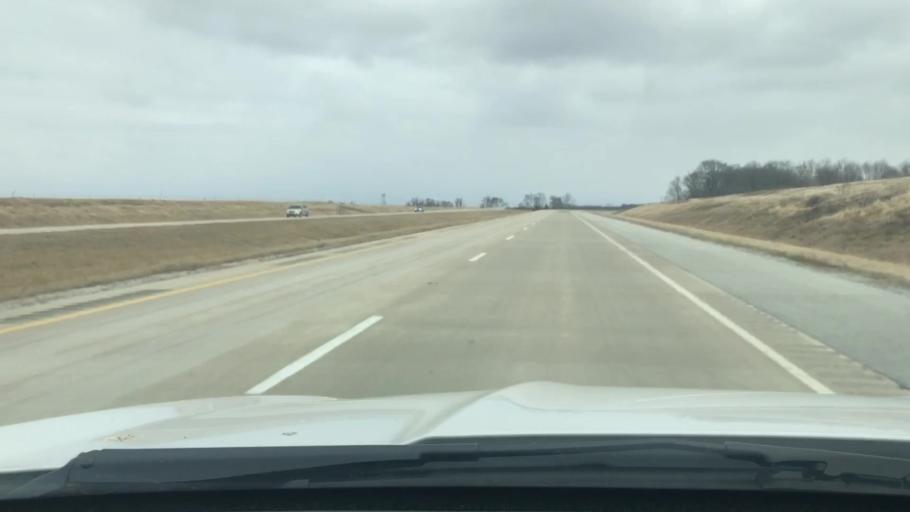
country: US
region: Indiana
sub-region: Carroll County
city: Delphi
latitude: 40.6215
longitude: -86.6298
